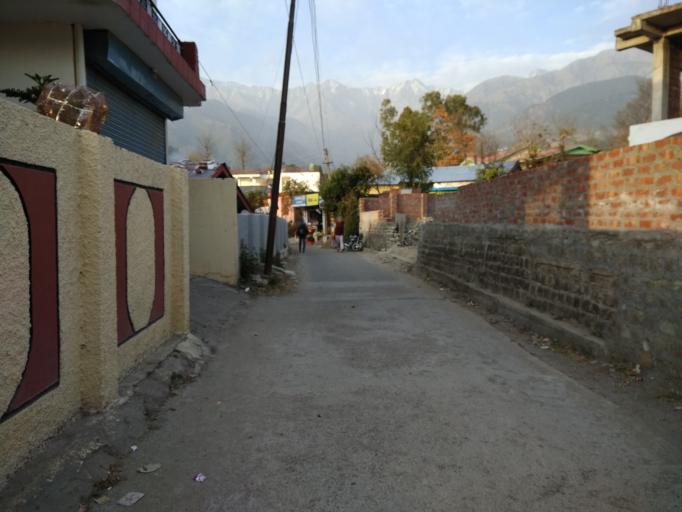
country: IN
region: Himachal Pradesh
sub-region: Kangra
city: Palampur
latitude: 32.1173
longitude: 76.5311
